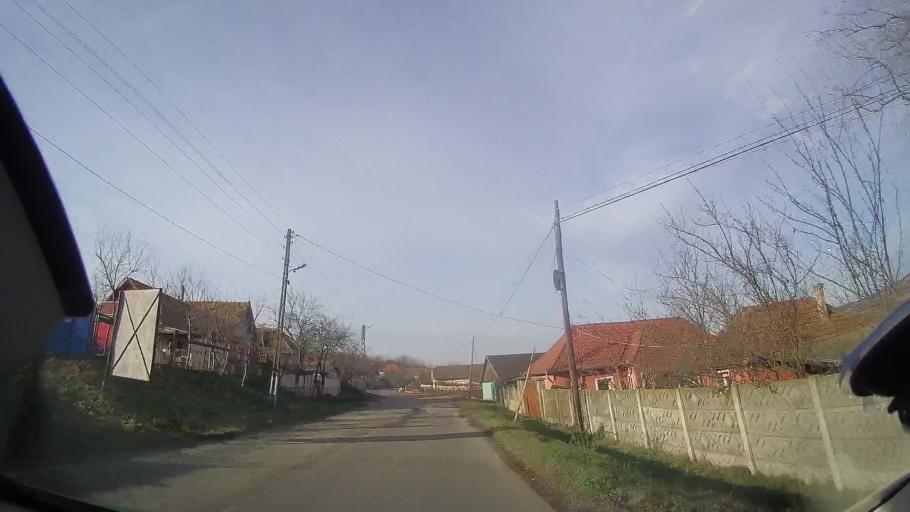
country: RO
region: Bihor
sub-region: Comuna Spinus
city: Spinus
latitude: 47.1809
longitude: 22.2121
